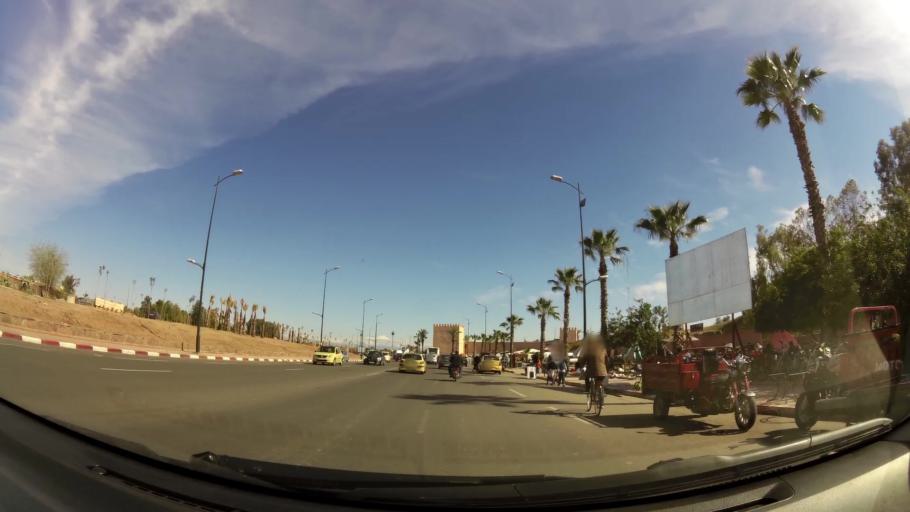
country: MA
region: Marrakech-Tensift-Al Haouz
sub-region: Marrakech
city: Marrakesh
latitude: 31.6414
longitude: -7.9844
